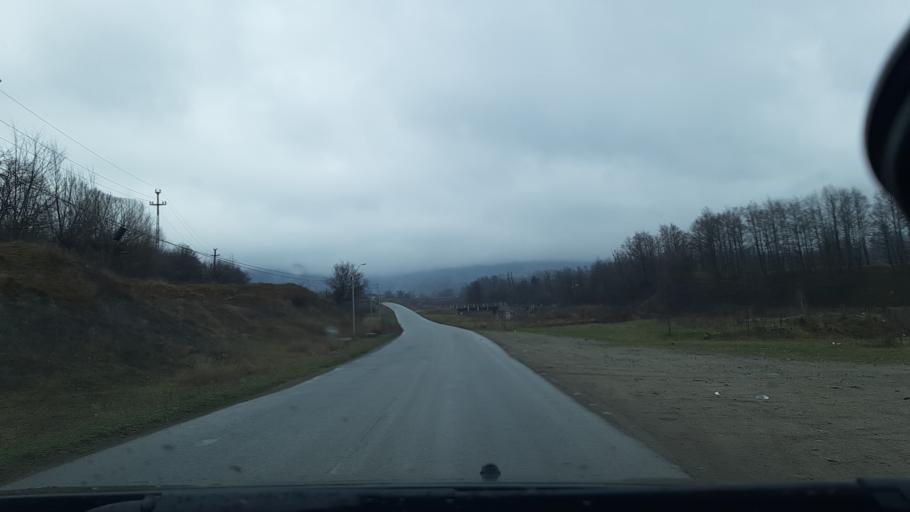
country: RO
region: Hunedoara
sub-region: Oras Petrila
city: Petrila
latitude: 45.4373
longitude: 23.4166
